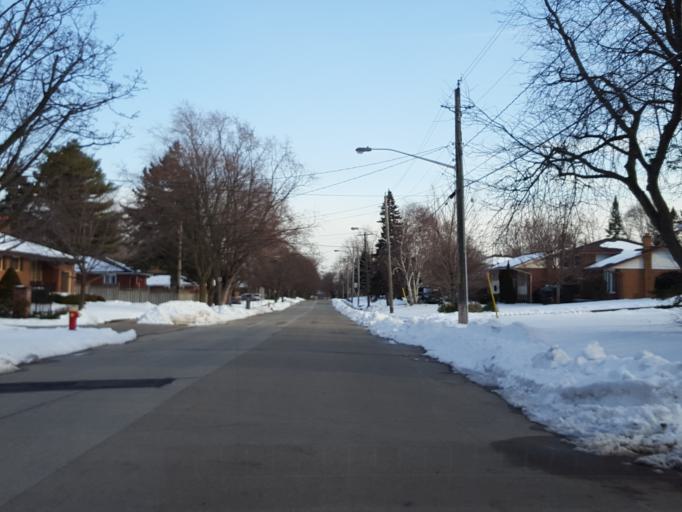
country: CA
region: Ontario
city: Burlington
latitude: 43.3463
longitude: -79.7857
